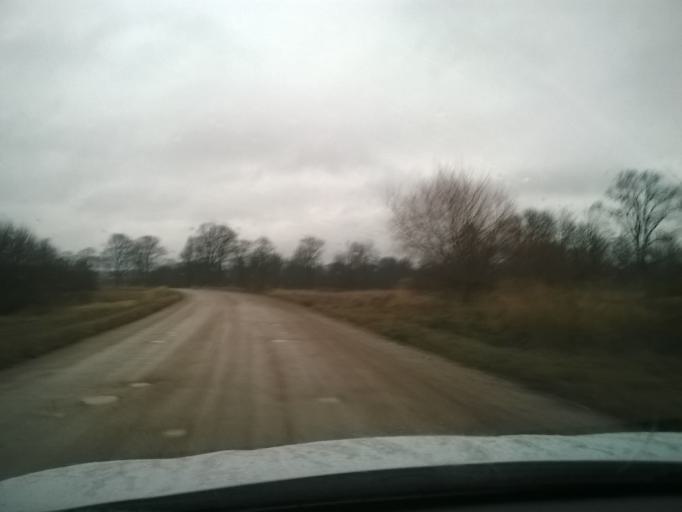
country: LV
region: Kandava
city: Kandava
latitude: 56.9802
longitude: 22.8577
